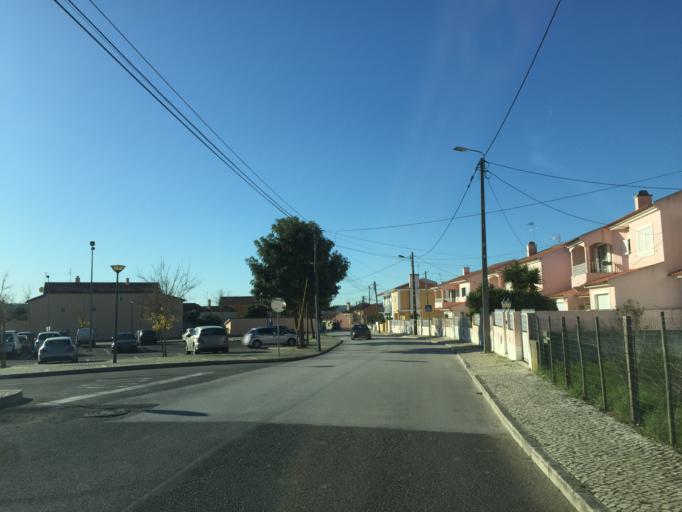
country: PT
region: Lisbon
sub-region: Sintra
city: Pero Pinheiro
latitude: 38.8581
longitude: -9.3220
